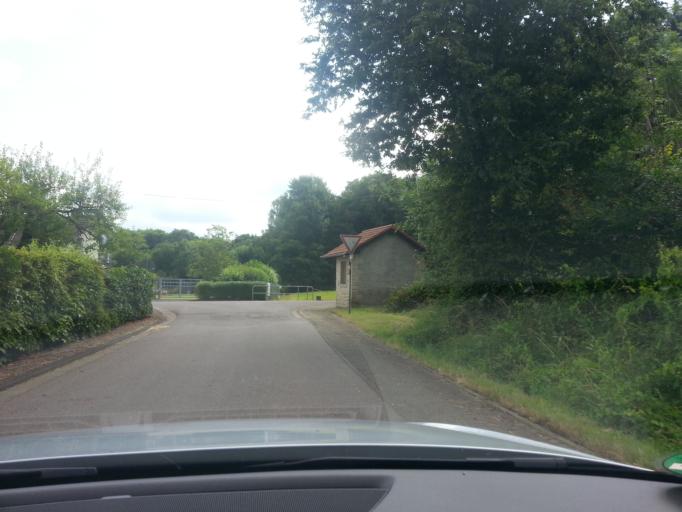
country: DE
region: Rheinland-Pfalz
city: Kirf
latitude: 49.5115
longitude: 6.4814
